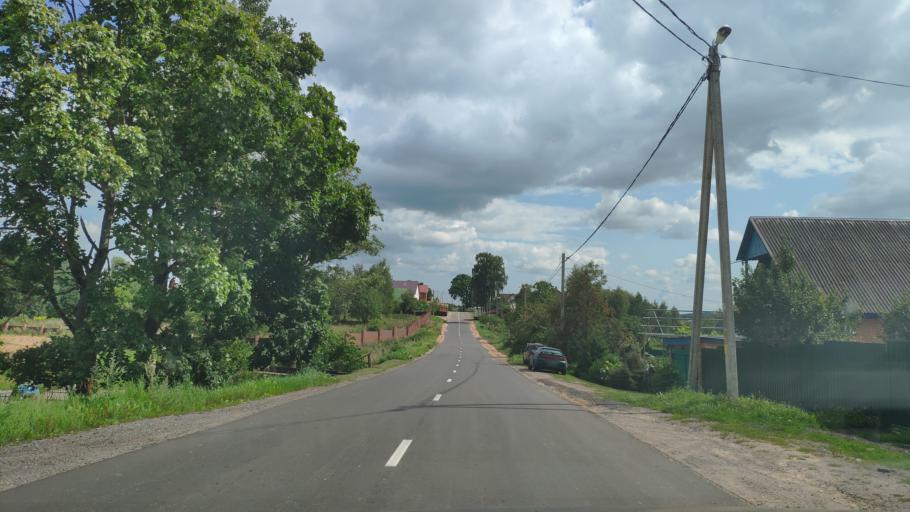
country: BY
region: Minsk
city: Khatsyezhyna
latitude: 53.8845
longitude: 27.2709
